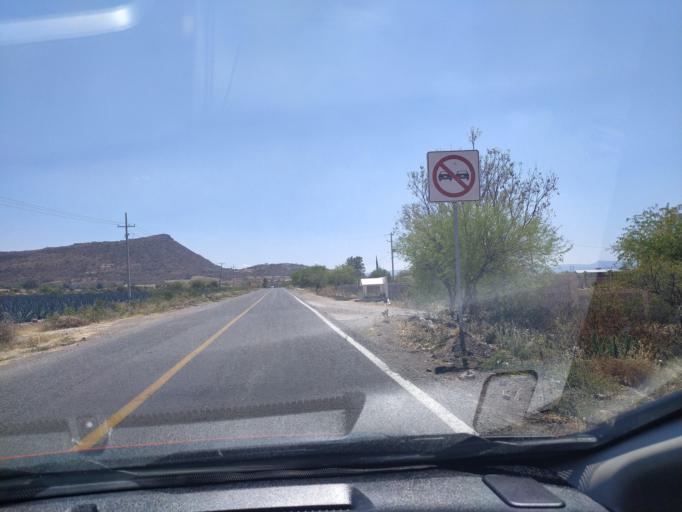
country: MX
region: Guanajuato
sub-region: San Francisco del Rincon
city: San Ignacio de Hidalgo
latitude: 20.8155
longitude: -101.8397
